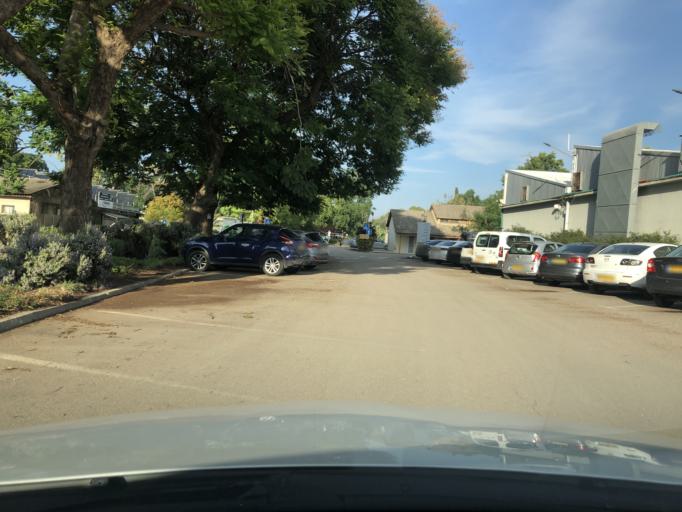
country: IL
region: Northern District
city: Yavne'el
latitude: 32.6574
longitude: 35.5806
